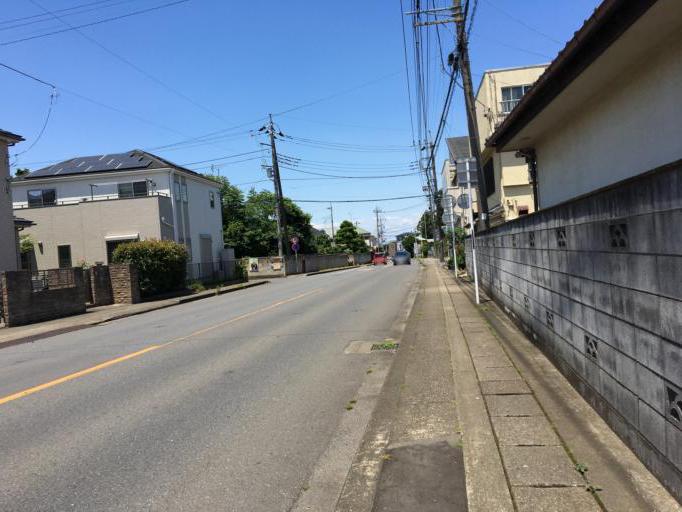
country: JP
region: Saitama
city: Sakado
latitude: 35.9396
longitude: 139.3887
